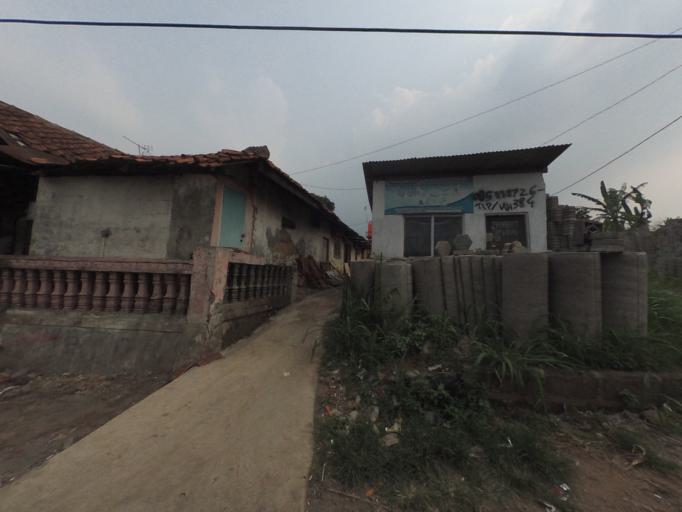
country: ID
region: West Java
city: Ciampea
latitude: -6.5634
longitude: 106.6816
